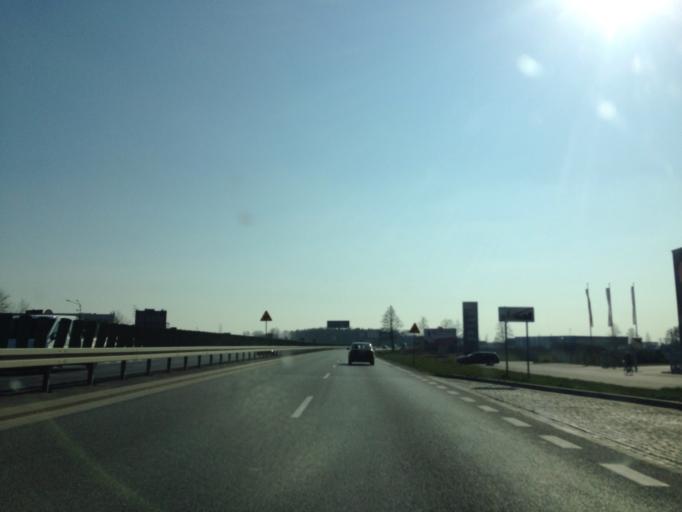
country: PL
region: Lower Silesian Voivodeship
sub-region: Powiat wroclawski
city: Dlugoleka
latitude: 51.1877
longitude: 17.2270
